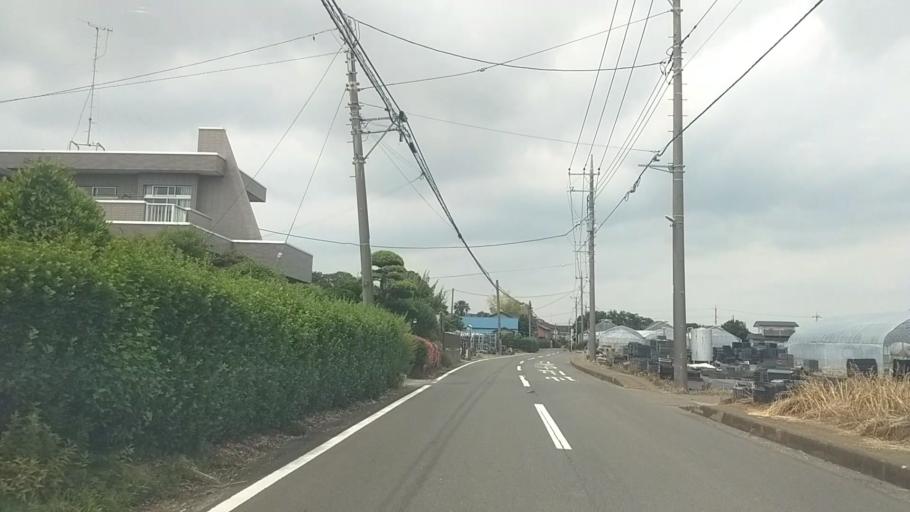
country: JP
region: Kanagawa
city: Chigasaki
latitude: 35.3896
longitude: 139.4141
